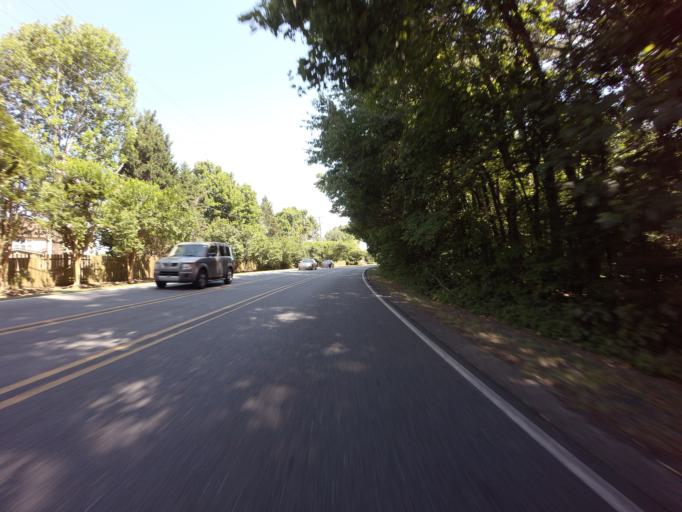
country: US
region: Georgia
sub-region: Fulton County
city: Johns Creek
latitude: 34.0820
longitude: -84.1853
